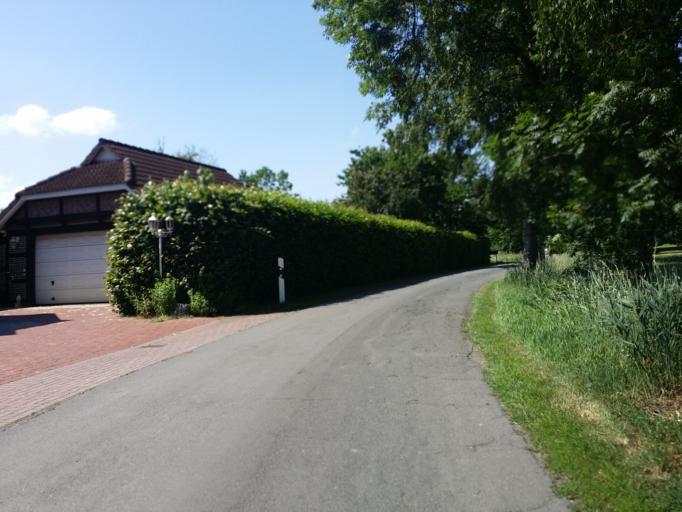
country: DE
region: Lower Saxony
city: Lemwerder
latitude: 53.1538
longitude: 8.5410
